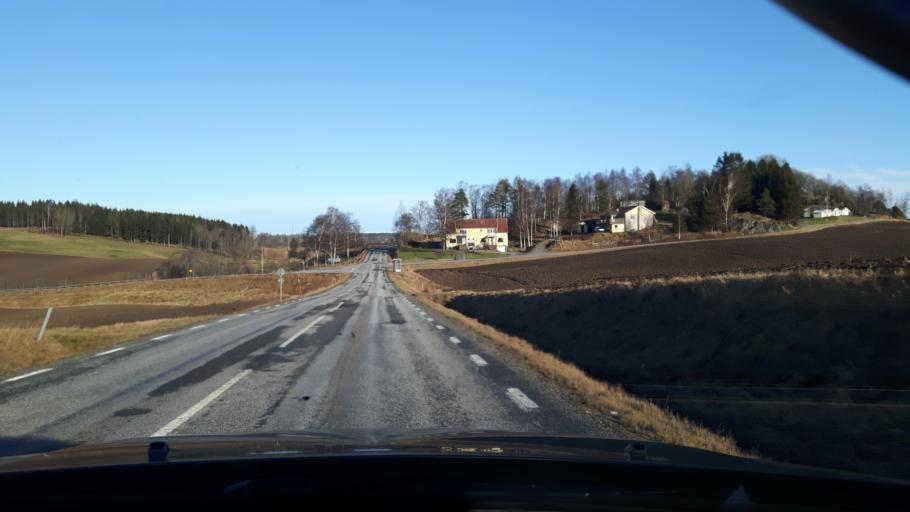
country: SE
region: Vaestra Goetaland
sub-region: Munkedals Kommun
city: Munkedal
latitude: 58.6164
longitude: 11.7620
